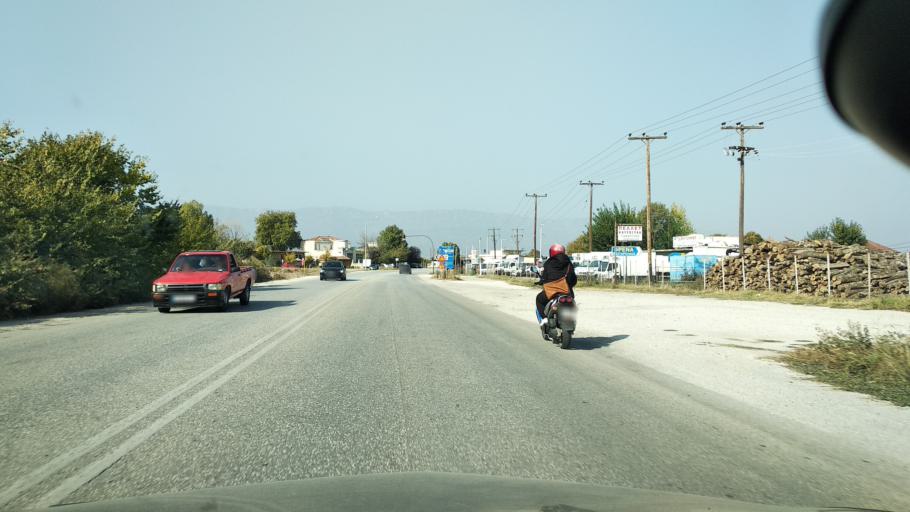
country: GR
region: Thessaly
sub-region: Trikala
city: Pyrgetos
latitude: 39.5715
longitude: 21.7505
